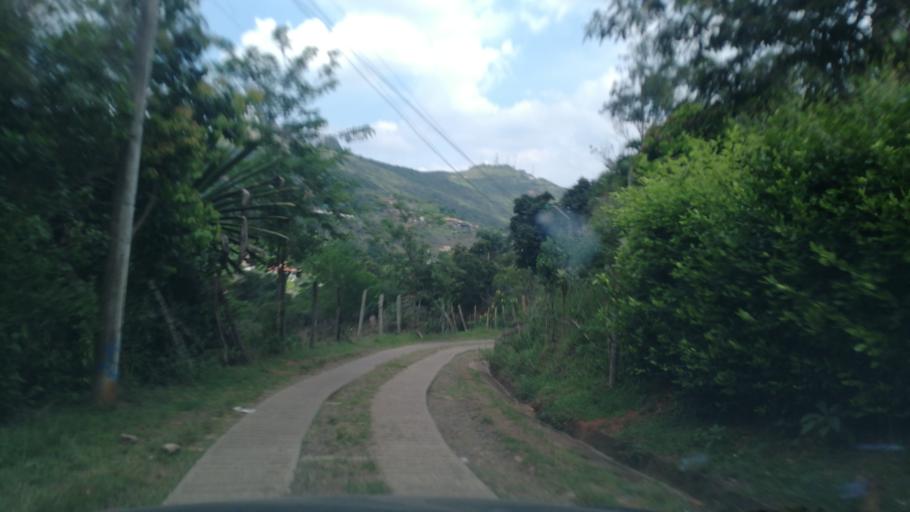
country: CO
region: Valle del Cauca
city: Cali
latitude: 3.4826
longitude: -76.5555
